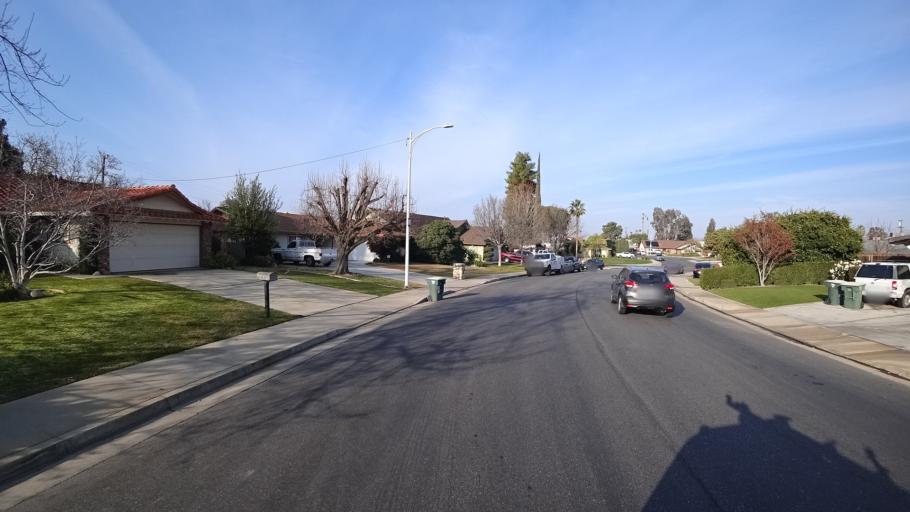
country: US
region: California
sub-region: Kern County
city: Oildale
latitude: 35.3999
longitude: -118.9474
